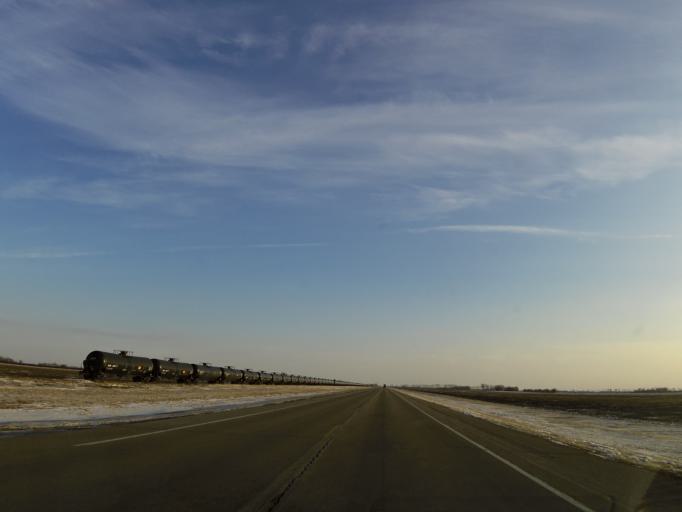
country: US
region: North Dakota
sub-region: Walsh County
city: Grafton
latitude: 48.4994
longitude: -97.4357
